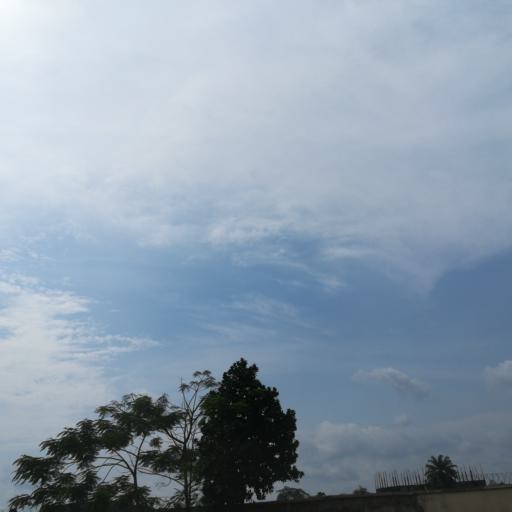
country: NG
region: Rivers
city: Port Harcourt
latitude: 4.8446
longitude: 7.0149
